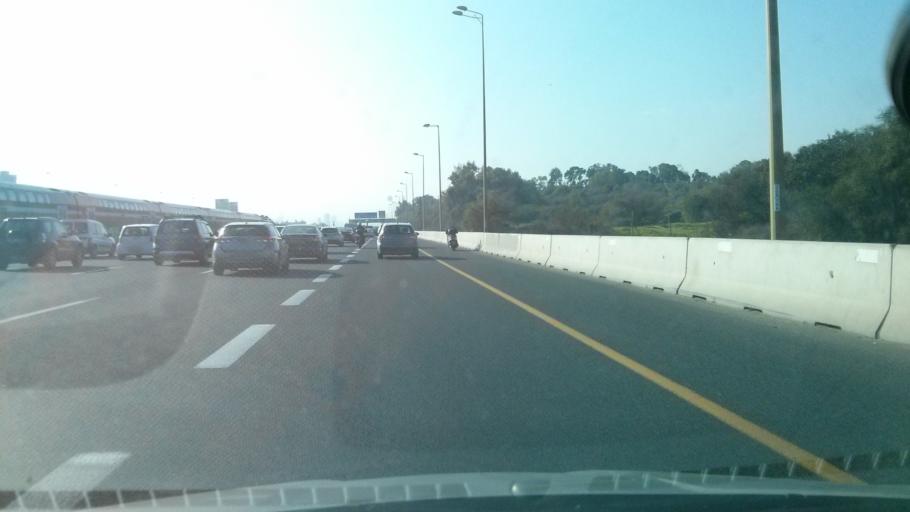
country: IL
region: Tel Aviv
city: Ramat HaSharon
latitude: 32.1305
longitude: 34.8097
